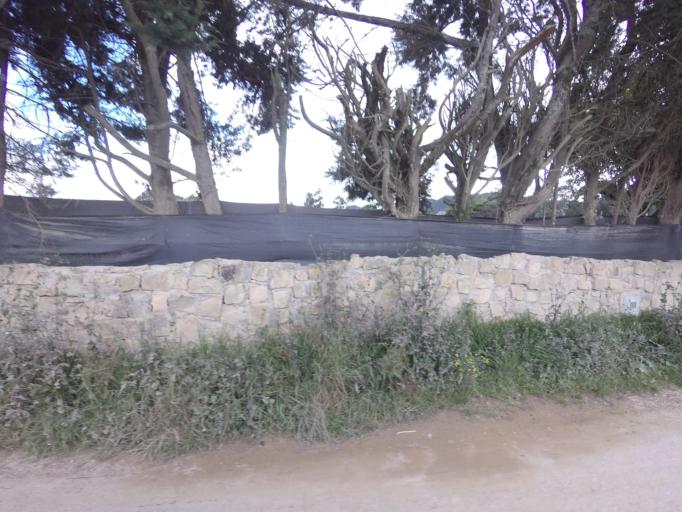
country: CO
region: Cundinamarca
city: Tabio
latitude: 4.9323
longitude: -74.0914
